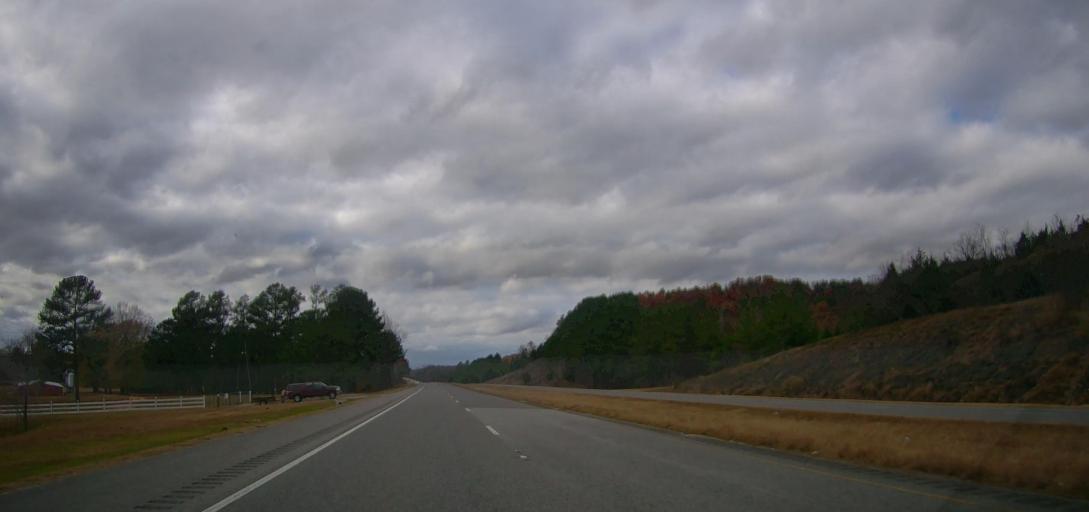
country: US
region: Alabama
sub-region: Lawrence County
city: Town Creek
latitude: 34.6256
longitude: -87.4754
